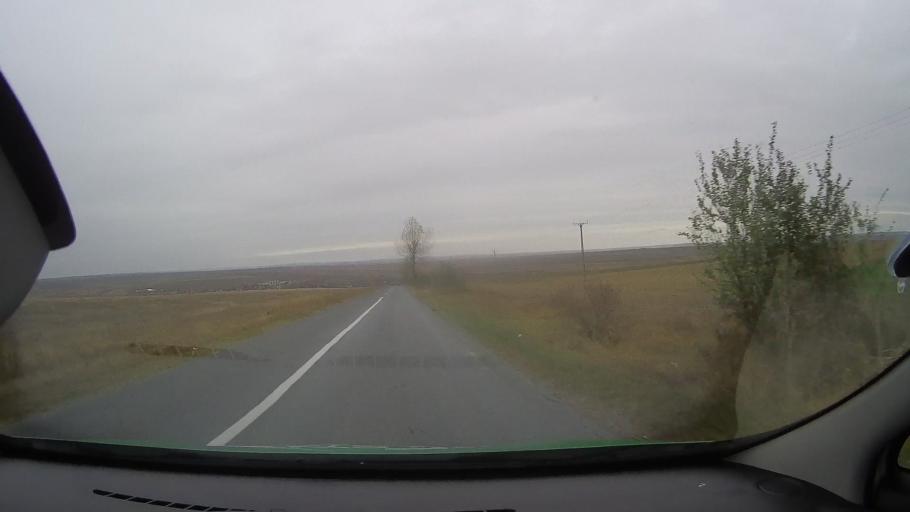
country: RO
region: Constanta
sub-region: Comuna Pantelimon
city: Pantelimon
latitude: 44.5891
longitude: 28.3174
